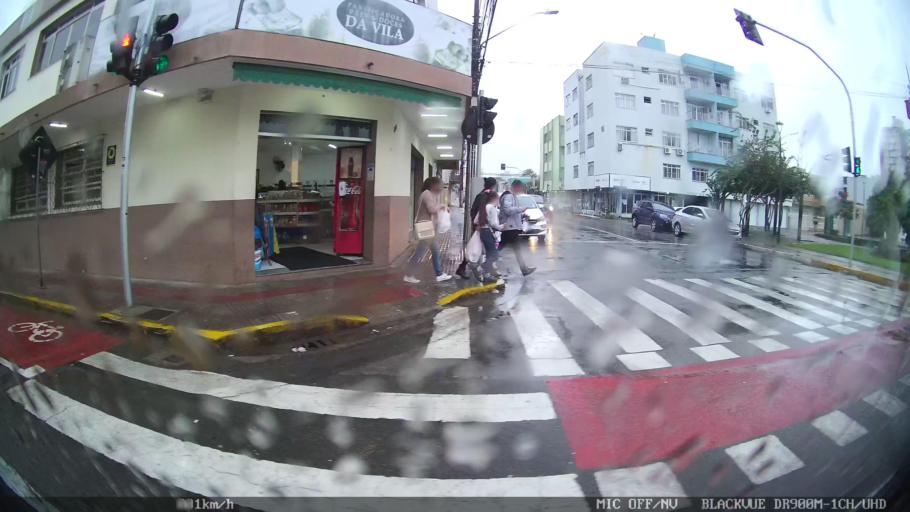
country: BR
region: Santa Catarina
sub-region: Itajai
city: Itajai
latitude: -26.9080
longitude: -48.6697
